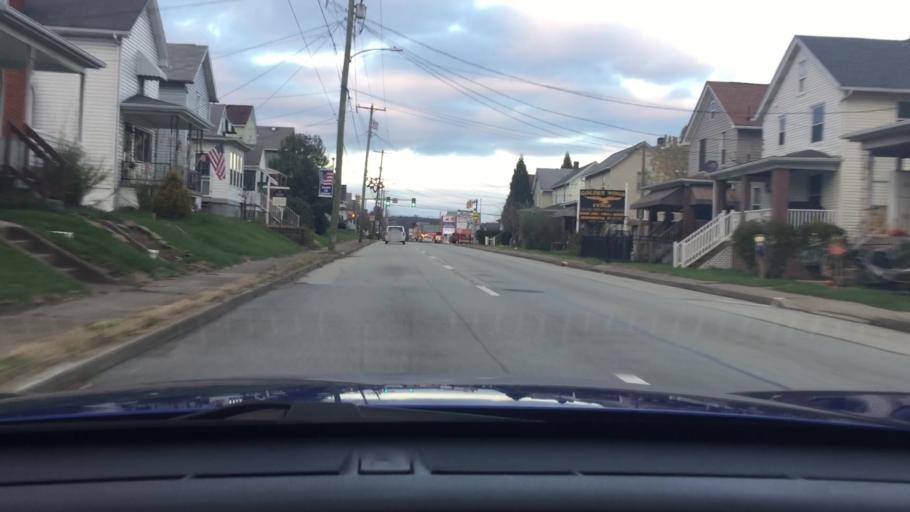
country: US
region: Pennsylvania
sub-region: Westmoreland County
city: Youngwood
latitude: 40.2359
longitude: -79.5808
